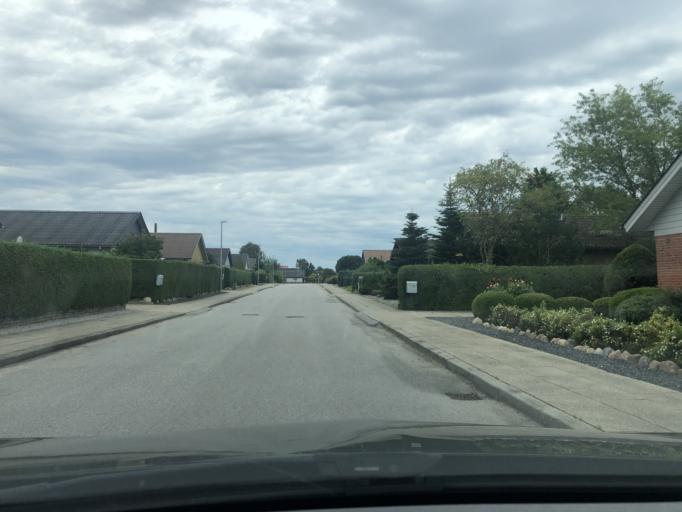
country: DK
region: South Denmark
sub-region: Varde Kommune
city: Olgod
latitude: 55.8061
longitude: 8.6109
